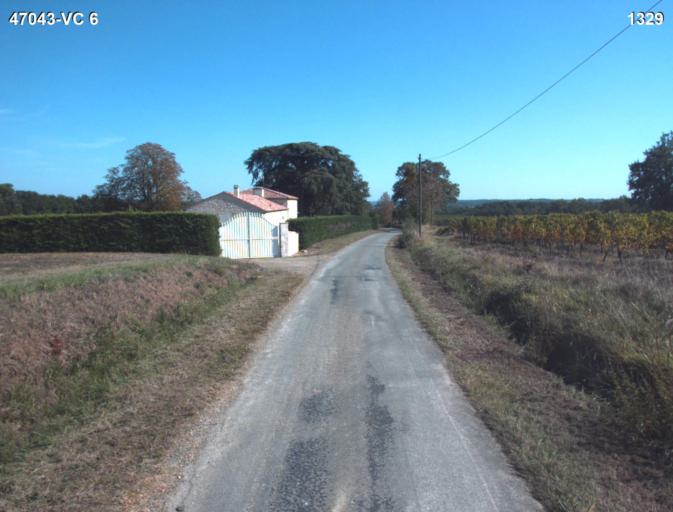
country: FR
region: Aquitaine
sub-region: Departement du Lot-et-Garonne
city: Buzet-sur-Baise
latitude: 44.2363
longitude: 0.3031
